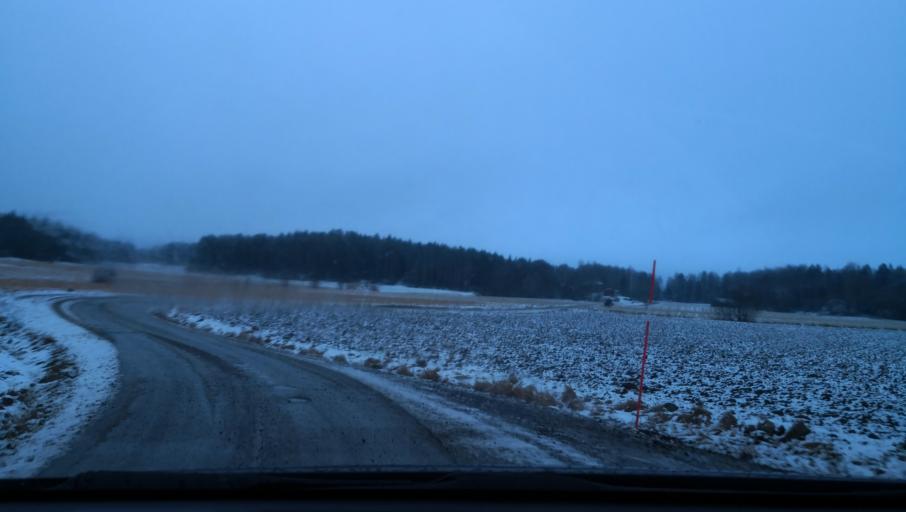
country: SE
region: Vaestmanland
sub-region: Kungsors Kommun
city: Kungsoer
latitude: 59.4008
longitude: 16.2046
